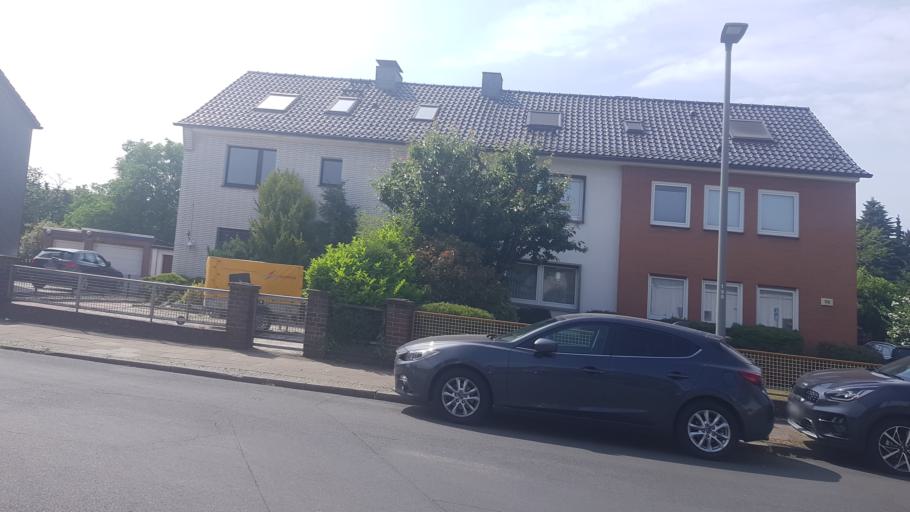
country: DE
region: North Rhine-Westphalia
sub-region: Regierungsbezirk Dusseldorf
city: Oberhausen
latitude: 51.4632
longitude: 6.8685
